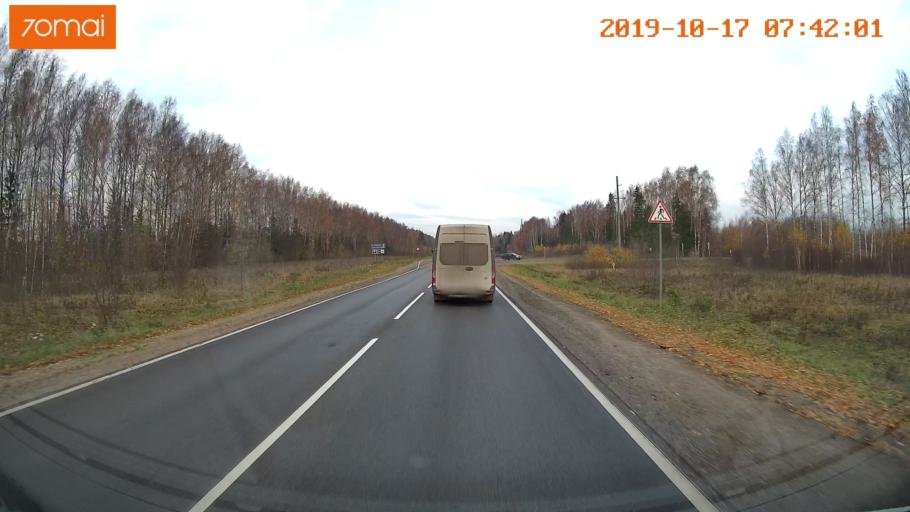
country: RU
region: Vladimir
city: Yur'yev-Pol'skiy
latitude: 56.4838
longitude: 39.7962
